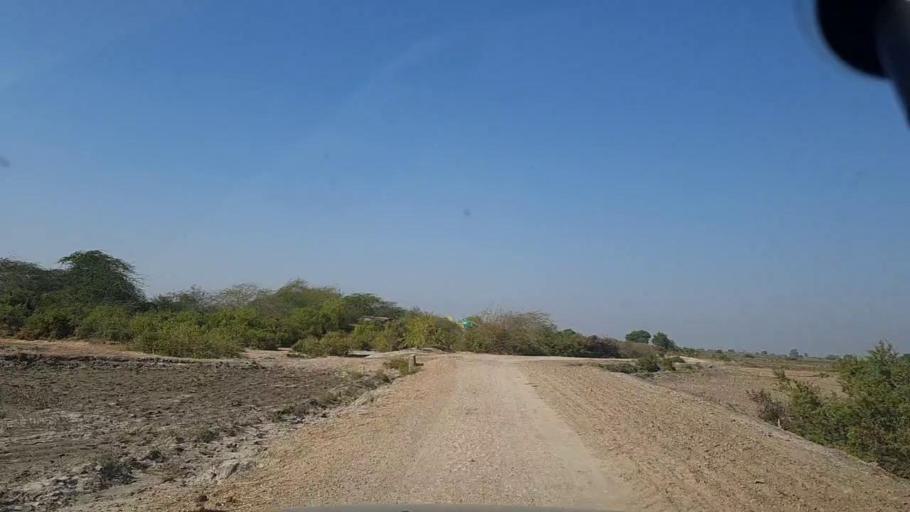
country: PK
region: Sindh
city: Chuhar Jamali
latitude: 24.5722
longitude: 68.0428
